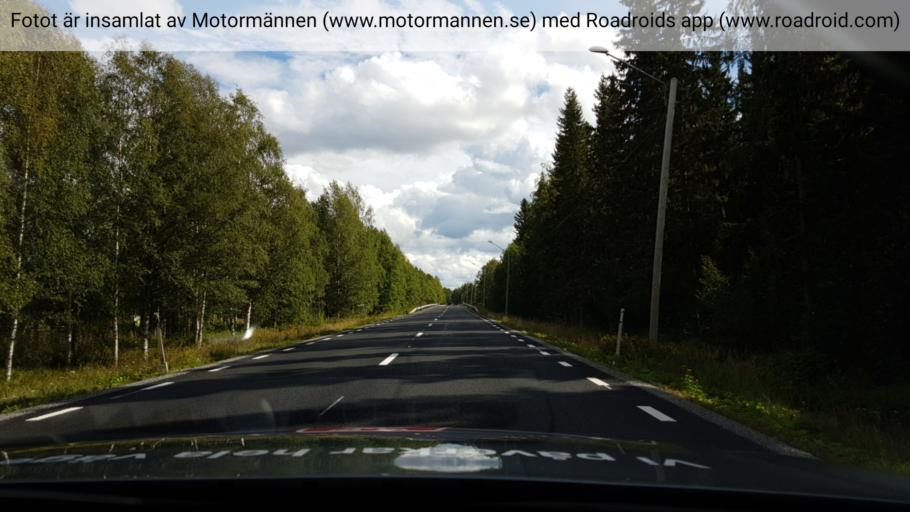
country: SE
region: Jaemtland
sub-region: OEstersunds Kommun
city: Brunflo
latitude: 63.1921
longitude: 15.1781
